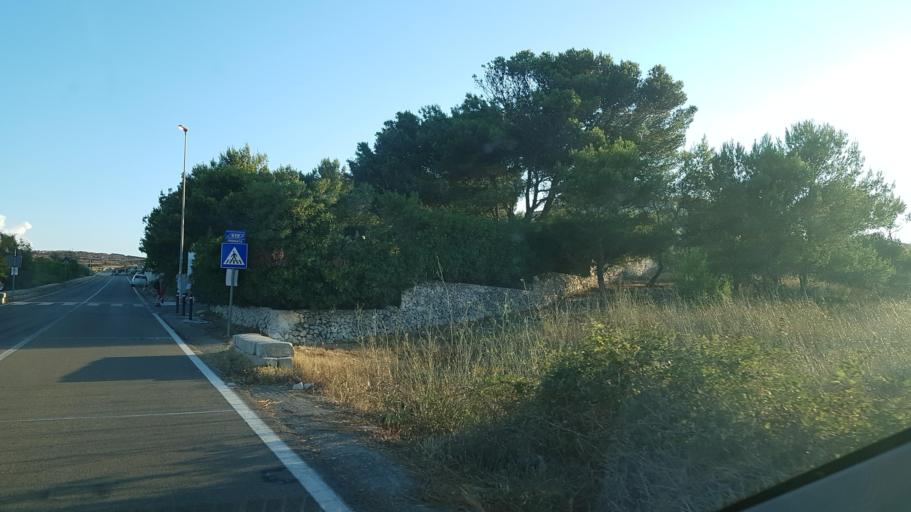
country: IT
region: Apulia
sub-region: Provincia di Lecce
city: Cerfignano
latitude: 40.0756
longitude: 18.4820
